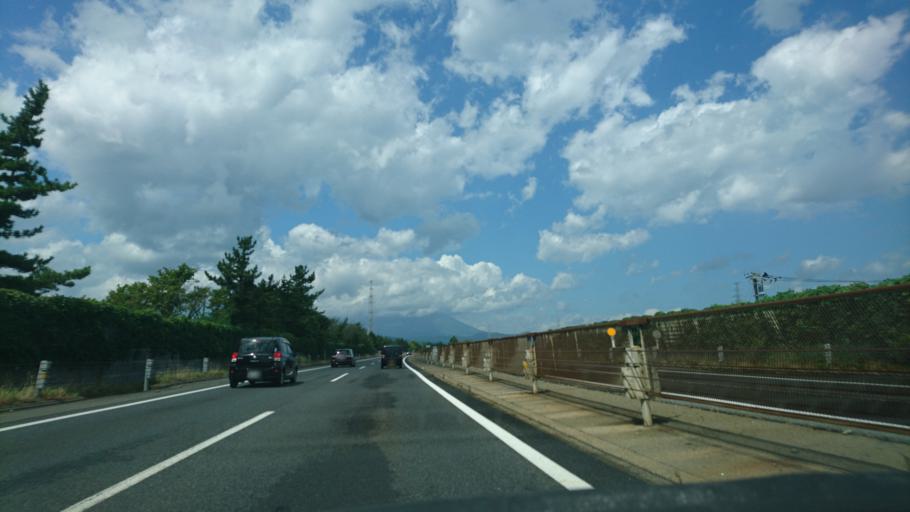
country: JP
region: Iwate
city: Morioka-shi
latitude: 39.6719
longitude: 141.1068
